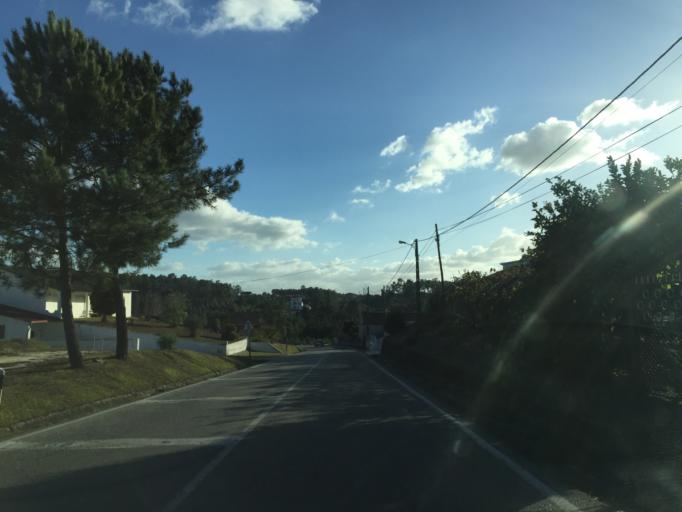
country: PT
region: Leiria
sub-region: Leiria
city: Monte Redondo
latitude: 39.9114
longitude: -8.8212
